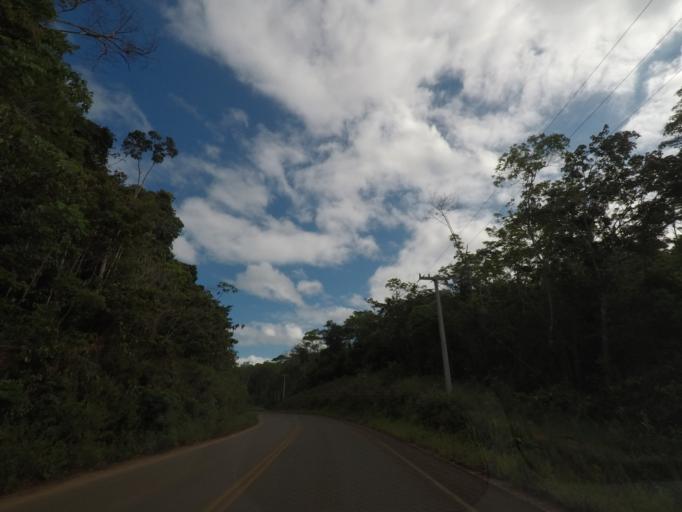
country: BR
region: Bahia
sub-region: Itacare
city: Itacare
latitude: -14.2249
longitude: -39.0972
